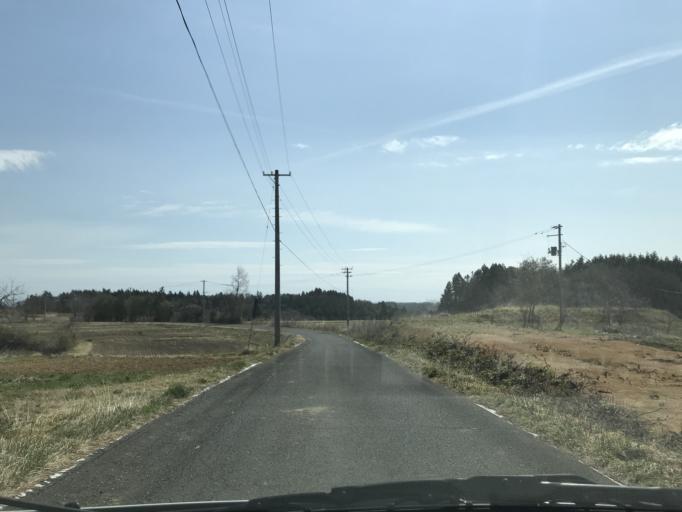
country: JP
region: Iwate
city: Ichinoseki
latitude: 38.8377
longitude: 141.1080
